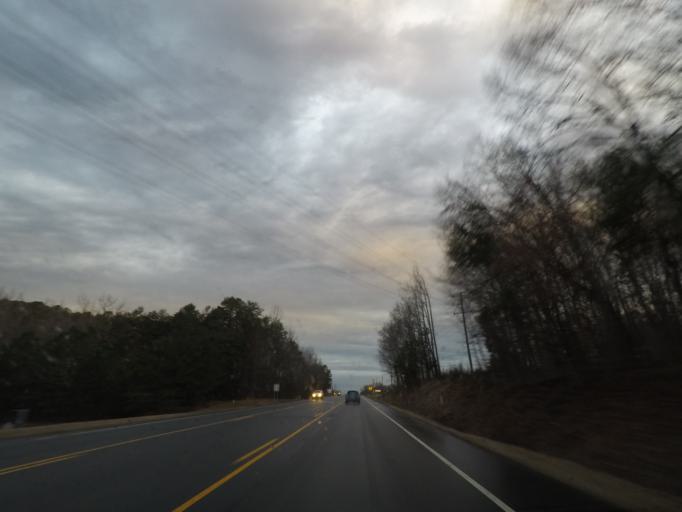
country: US
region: North Carolina
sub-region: Caswell County
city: Yanceyville
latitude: 36.4126
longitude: -79.3443
